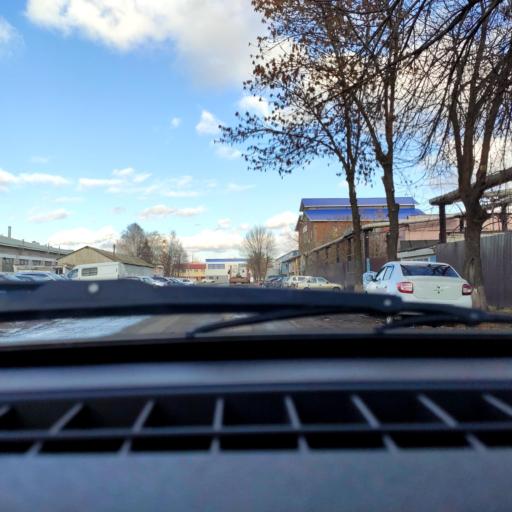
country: RU
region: Bashkortostan
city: Ufa
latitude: 54.7846
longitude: 56.0619
